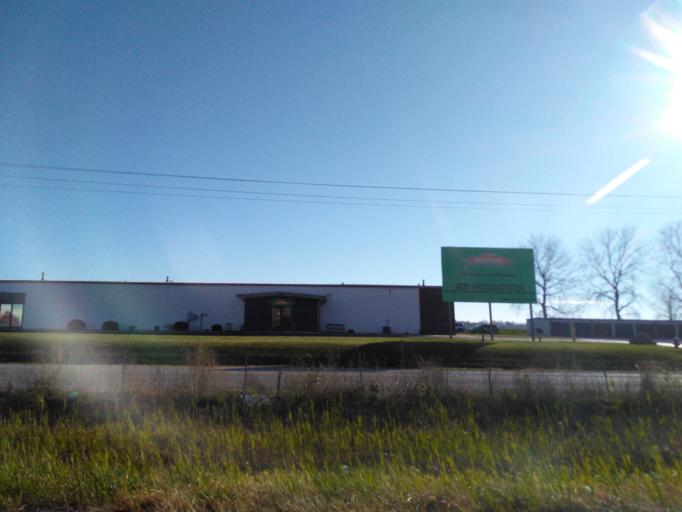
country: US
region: Illinois
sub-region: Madison County
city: Troy
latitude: 38.7404
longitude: -89.9101
